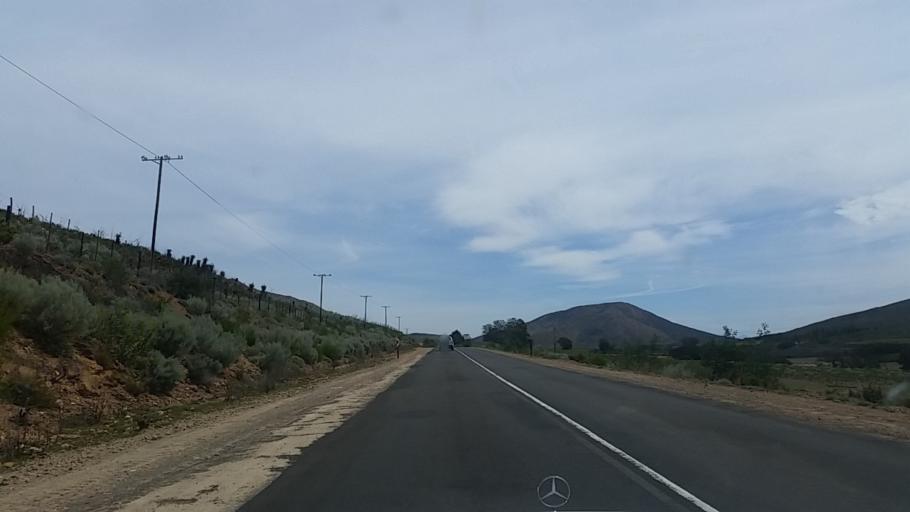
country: ZA
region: Western Cape
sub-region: Eden District Municipality
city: George
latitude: -33.8199
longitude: 22.3696
